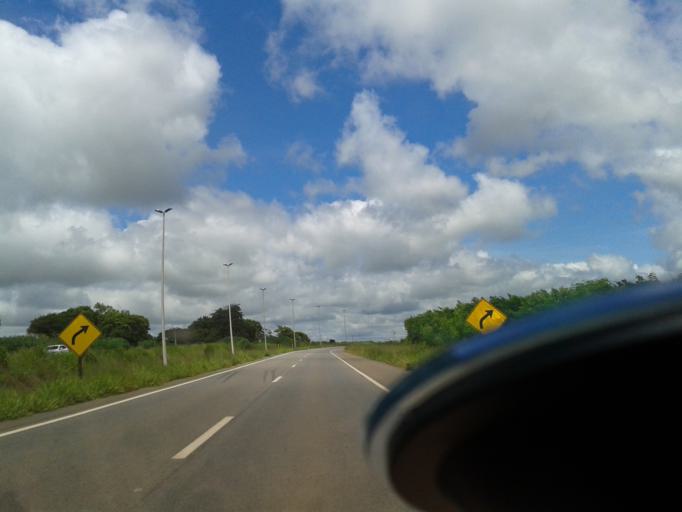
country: BR
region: Goias
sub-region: Itaberai
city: Itaberai
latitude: -16.0684
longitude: -49.7721
